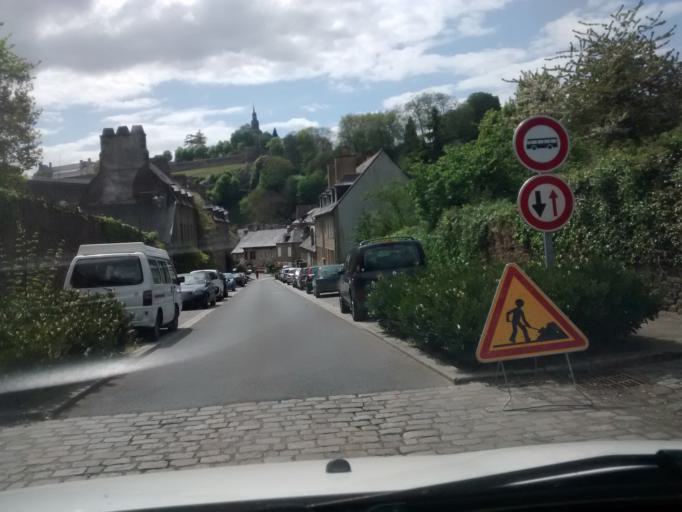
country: FR
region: Brittany
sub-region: Departement des Cotes-d'Armor
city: Dinan
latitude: 48.4571
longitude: -2.0357
